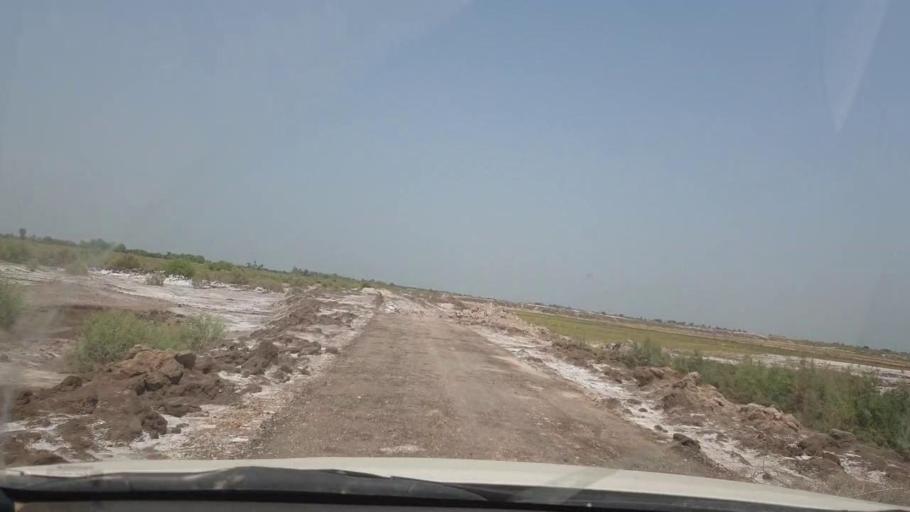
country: PK
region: Sindh
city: Lakhi
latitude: 27.8884
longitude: 68.7488
